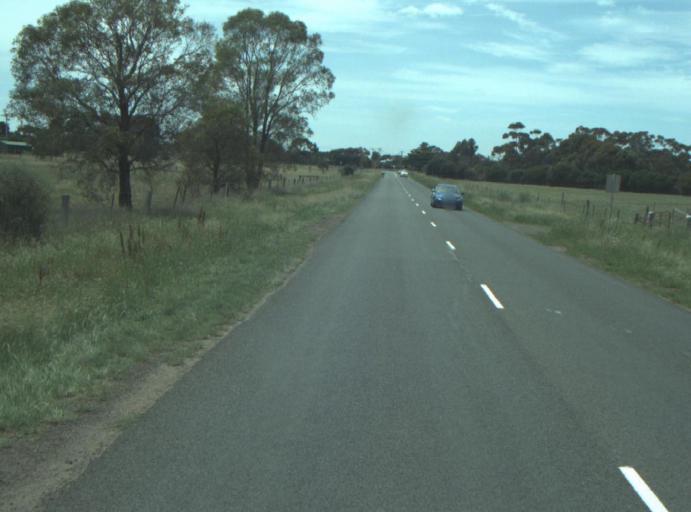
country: AU
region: Victoria
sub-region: Greater Geelong
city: Lara
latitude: -38.0226
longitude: 144.3730
